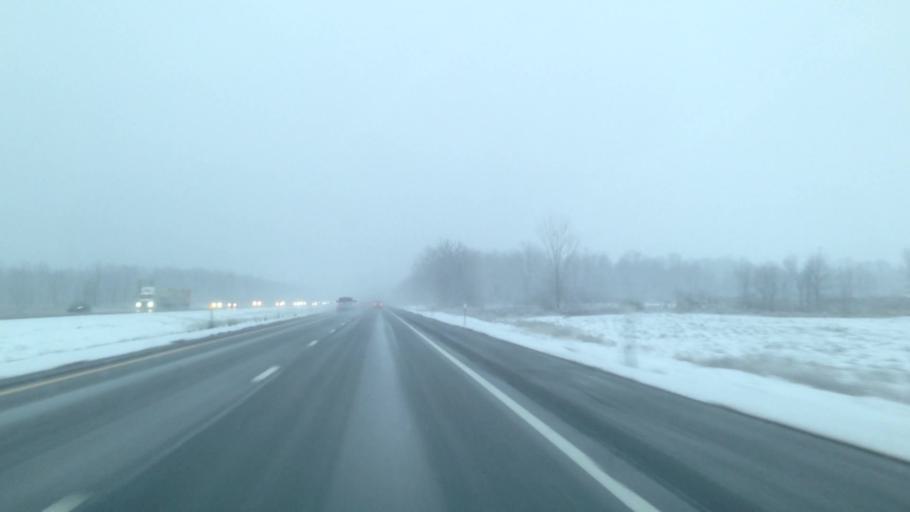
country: US
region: New York
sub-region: Madison County
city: Chittenango
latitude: 43.0938
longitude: -75.8228
